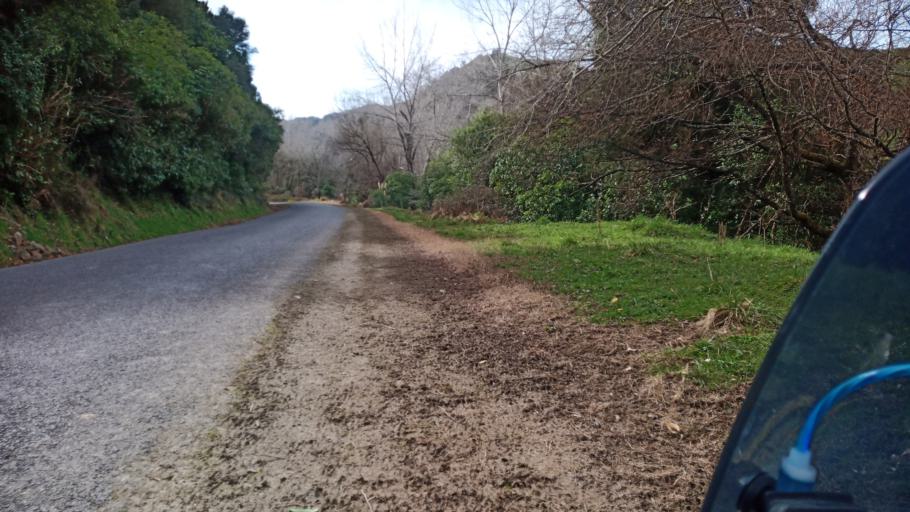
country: NZ
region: Hawke's Bay
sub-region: Wairoa District
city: Wairoa
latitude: -38.7996
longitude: 177.4455
